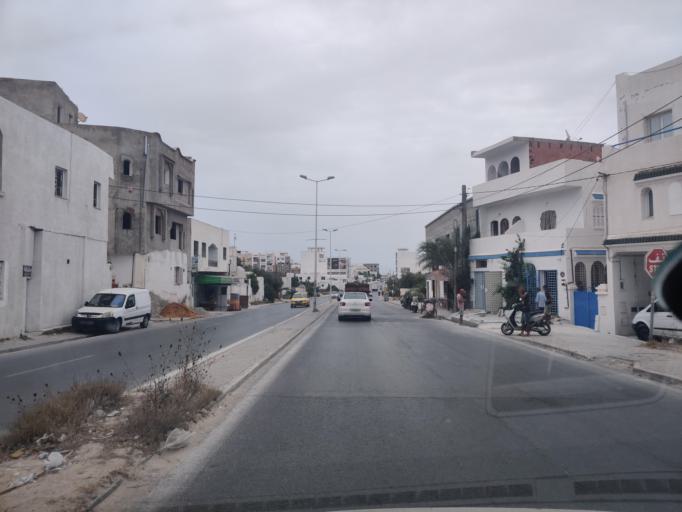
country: TN
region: Nabul
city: Al Hammamat
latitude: 36.4091
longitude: 10.6248
